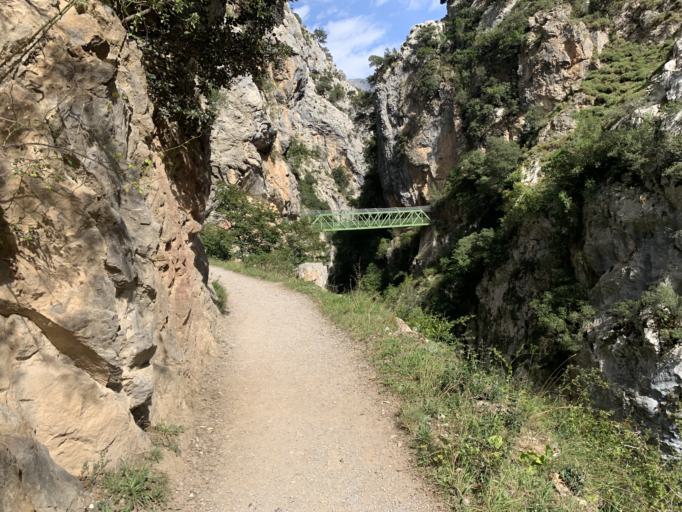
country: ES
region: Castille and Leon
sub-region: Provincia de Leon
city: Posada de Valdeon
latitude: 43.2237
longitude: -4.8959
